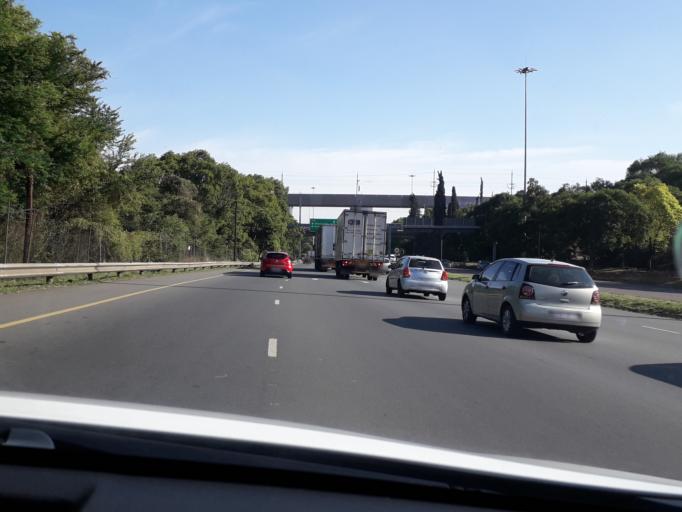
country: ZA
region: Gauteng
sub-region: City of Tshwane Metropolitan Municipality
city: Pretoria
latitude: -25.7661
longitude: 28.1949
